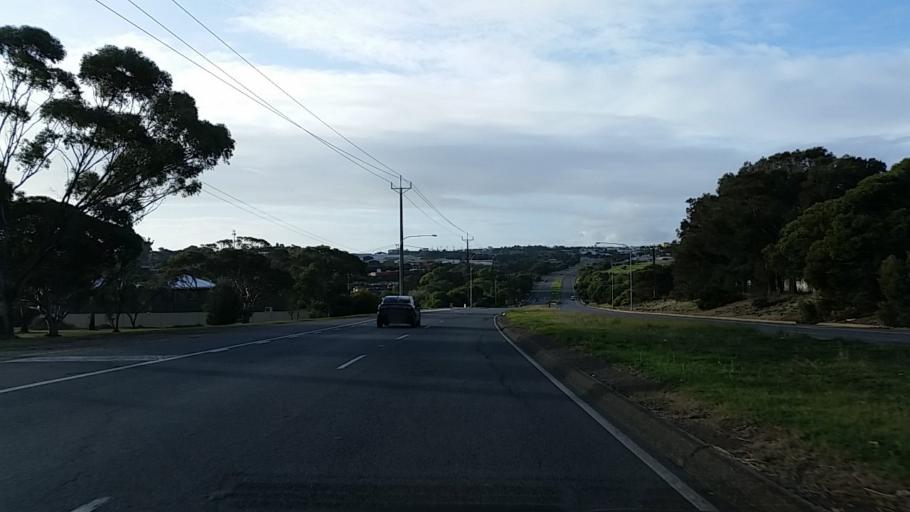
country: AU
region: South Australia
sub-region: Adelaide
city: Port Noarlunga
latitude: -35.1269
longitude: 138.4857
